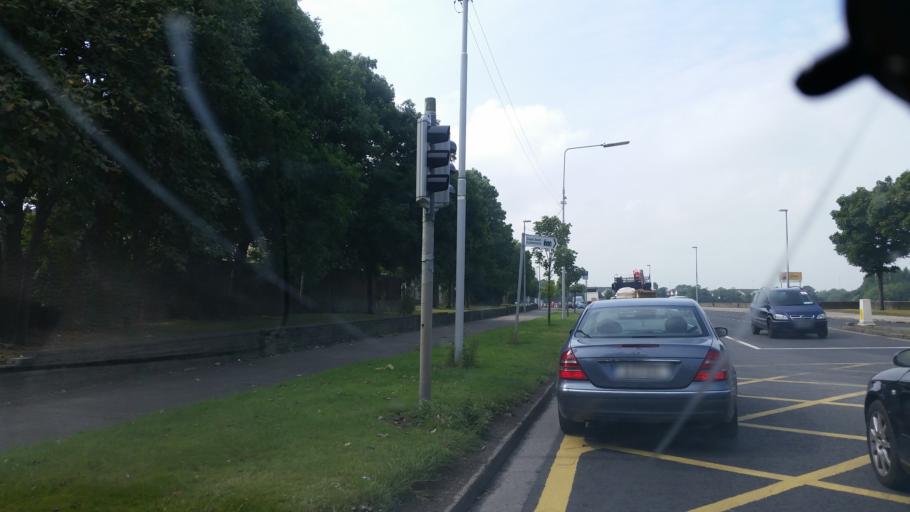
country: IE
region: Leinster
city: Artane
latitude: 53.3973
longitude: -6.2196
